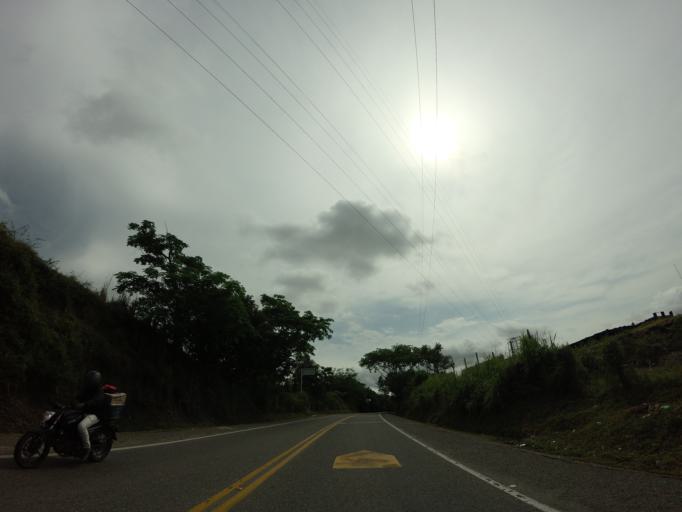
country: CO
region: Caldas
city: La Dorada
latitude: 5.4439
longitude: -74.6774
